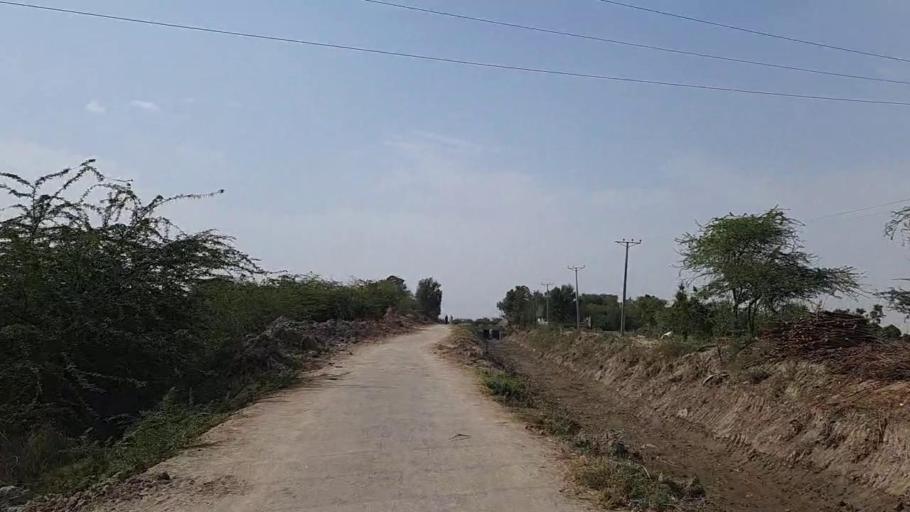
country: PK
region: Sindh
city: Daro Mehar
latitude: 24.8016
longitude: 68.1840
